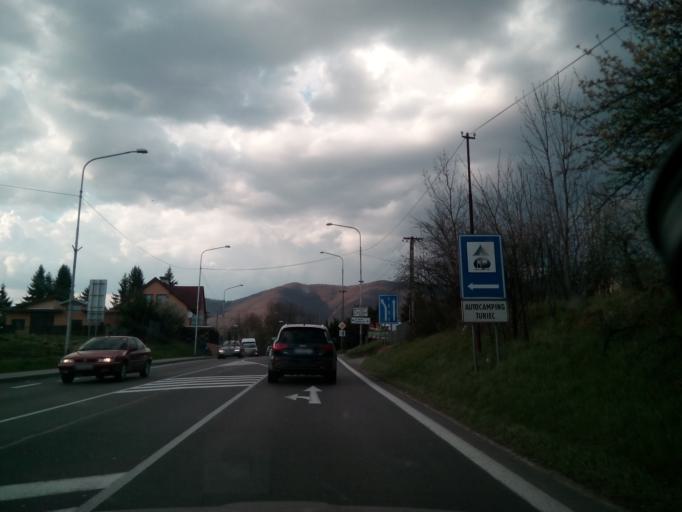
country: SK
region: Zilinsky
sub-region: Okres Zilina
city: Vrutky
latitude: 49.1075
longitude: 18.9177
